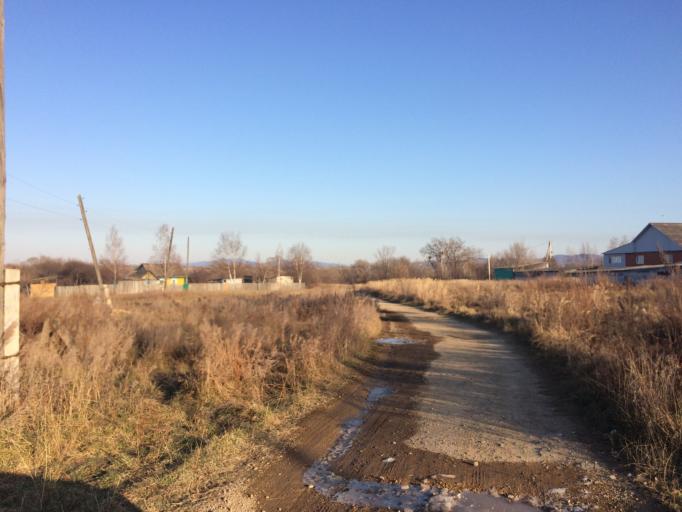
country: RU
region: Primorskiy
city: Ivanovka
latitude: 43.9568
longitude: 132.4719
